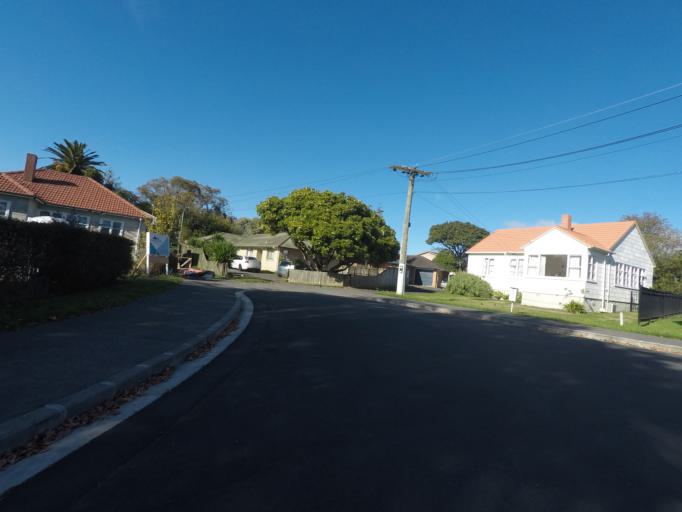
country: NZ
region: Auckland
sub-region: Auckland
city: Rosebank
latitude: -36.8934
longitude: 174.7091
